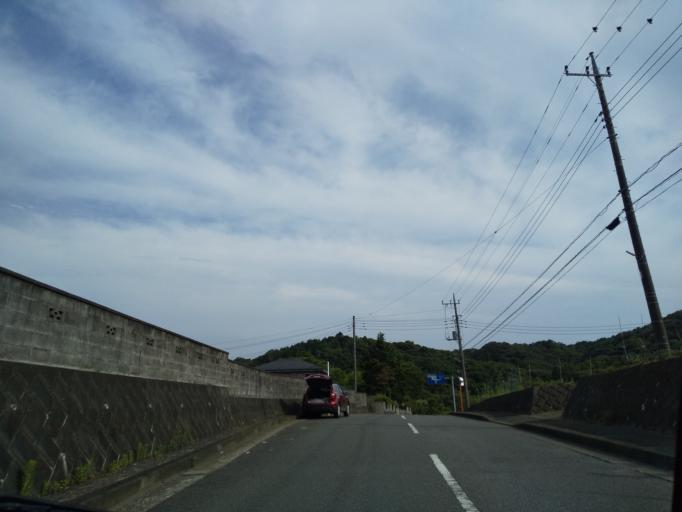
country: JP
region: Kanagawa
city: Atsugi
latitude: 35.4925
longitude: 139.3153
